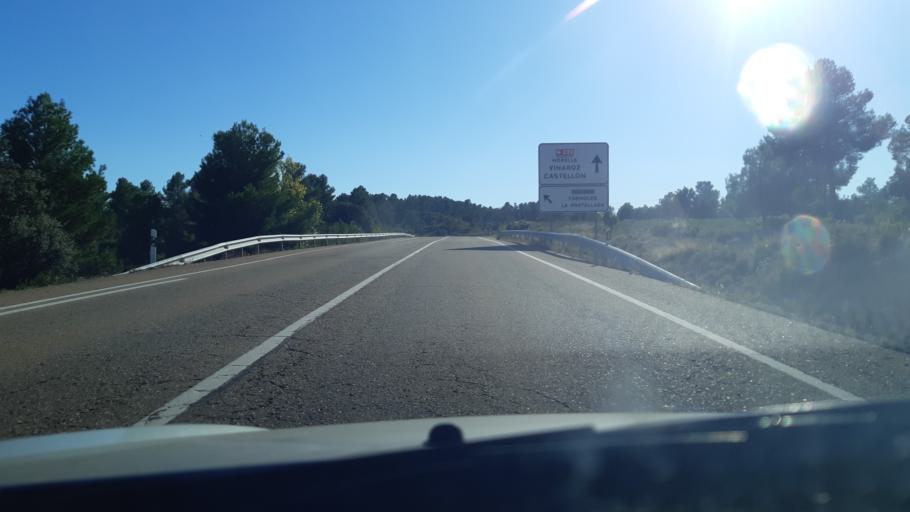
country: ES
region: Aragon
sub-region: Provincia de Teruel
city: Fornoles
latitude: 40.9170
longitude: -0.0194
